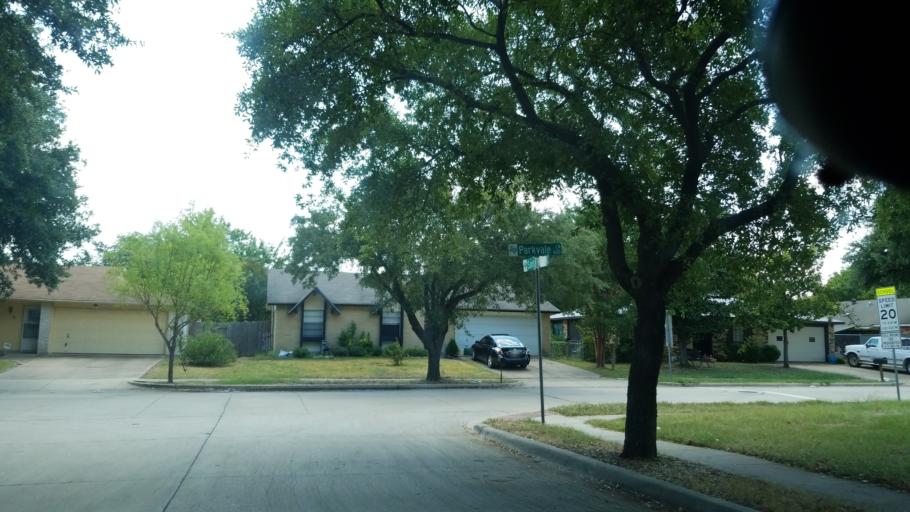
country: US
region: Texas
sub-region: Dallas County
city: Grand Prairie
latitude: 32.7019
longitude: -96.9959
